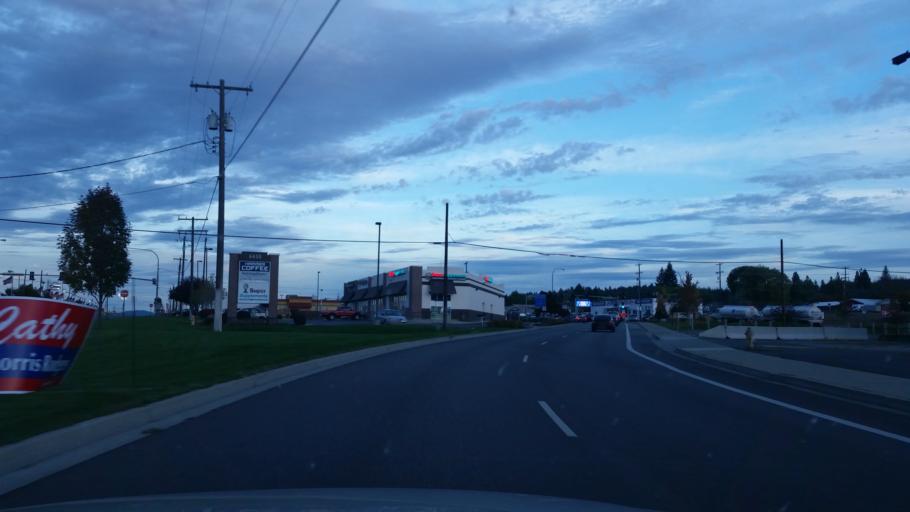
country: US
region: Washington
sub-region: Spokane County
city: Dishman
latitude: 47.6568
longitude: -117.3170
